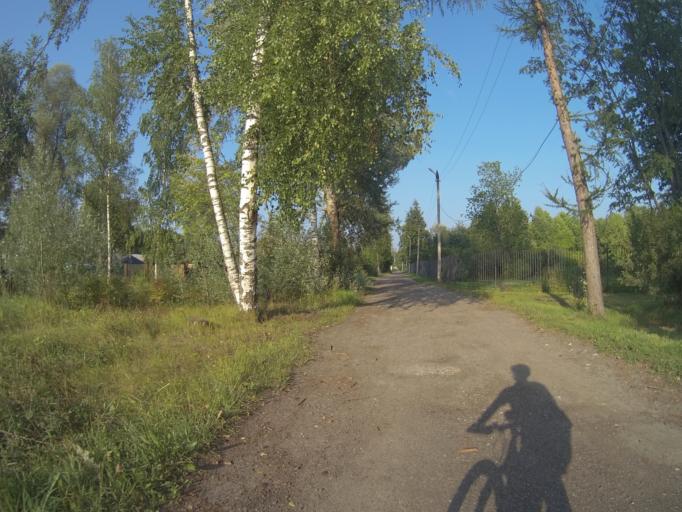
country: RU
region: Vladimir
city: Sudogda
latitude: 56.0437
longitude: 40.8323
